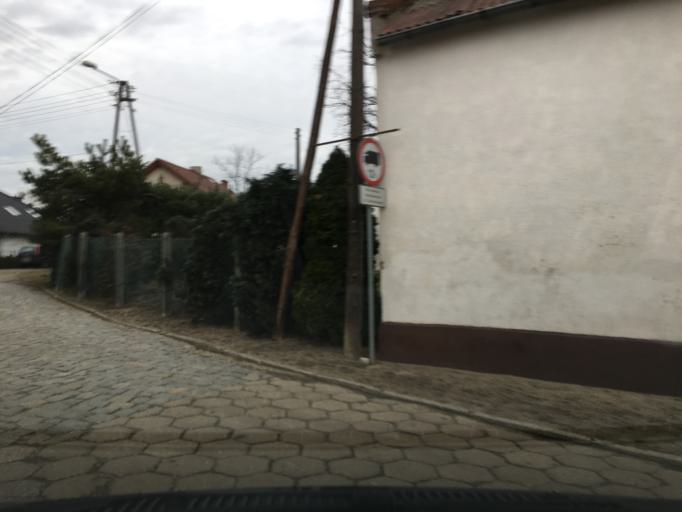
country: PL
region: Opole Voivodeship
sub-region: Powiat kedzierzynsko-kozielski
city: Wiekszyce
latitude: 50.3529
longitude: 18.1221
